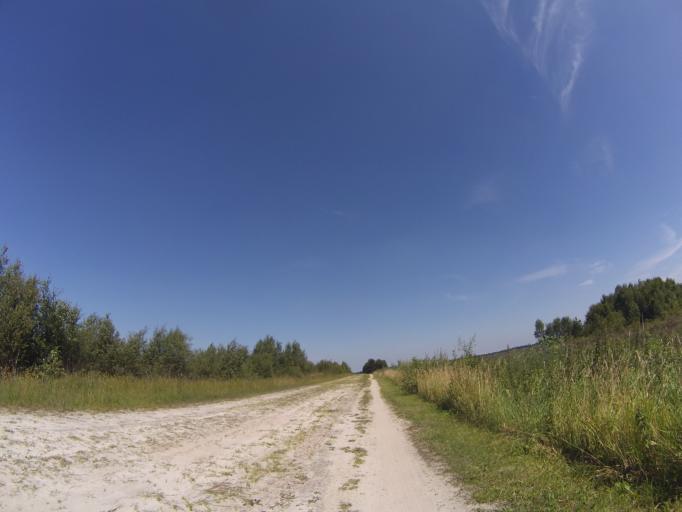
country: DE
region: Lower Saxony
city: Twist
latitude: 52.6982
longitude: 7.0611
